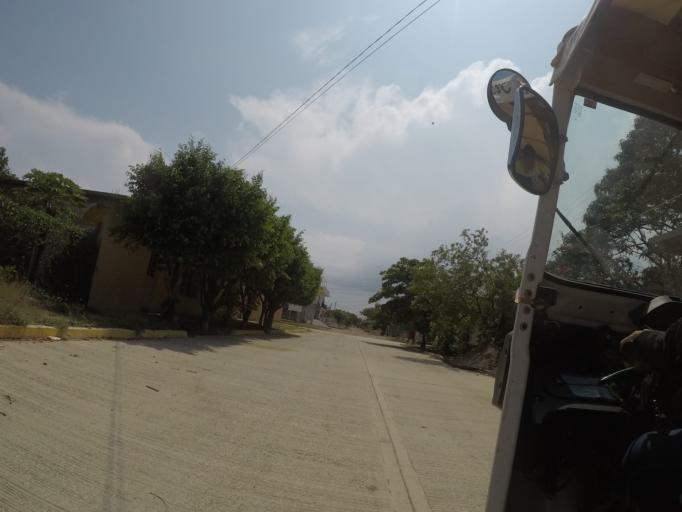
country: MX
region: Oaxaca
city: Union Hidalgo
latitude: 16.4746
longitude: -94.8349
